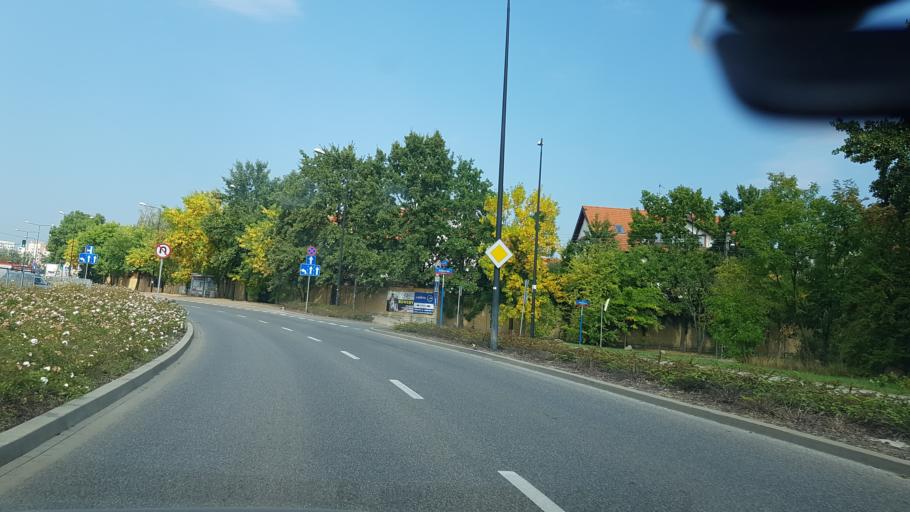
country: PL
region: Masovian Voivodeship
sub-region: Warszawa
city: Ursynow
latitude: 52.1672
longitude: 21.0449
